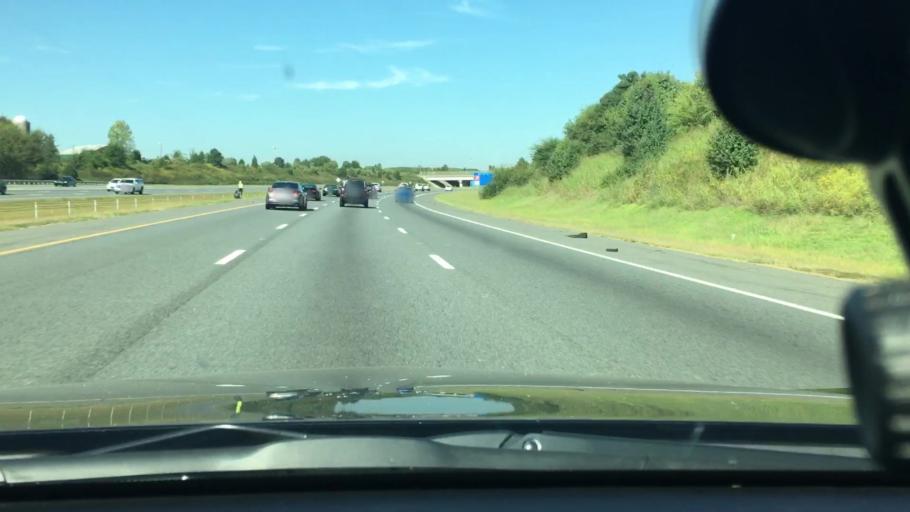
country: US
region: North Carolina
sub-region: Cabarrus County
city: Harrisburg
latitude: 35.3092
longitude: -80.7028
